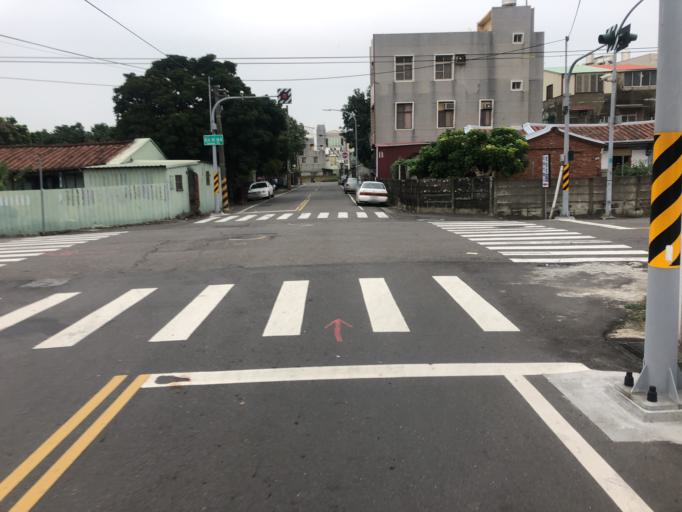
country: TW
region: Taiwan
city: Xinying
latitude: 23.1813
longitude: 120.2457
